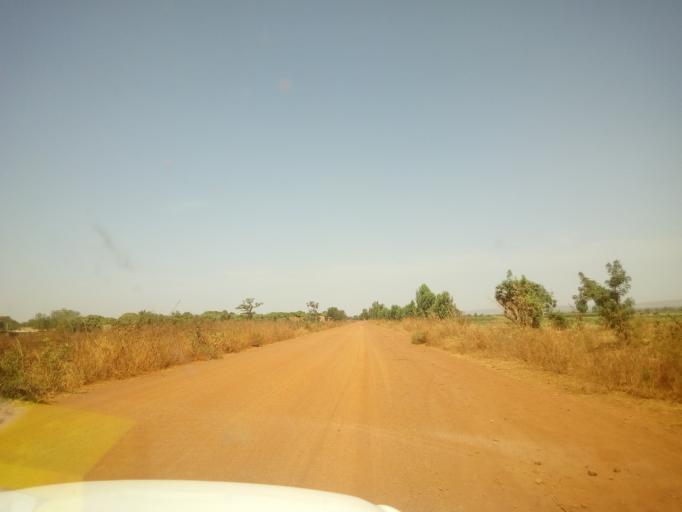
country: ML
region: Bamako
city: Bamako
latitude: 12.6203
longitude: -7.7757
